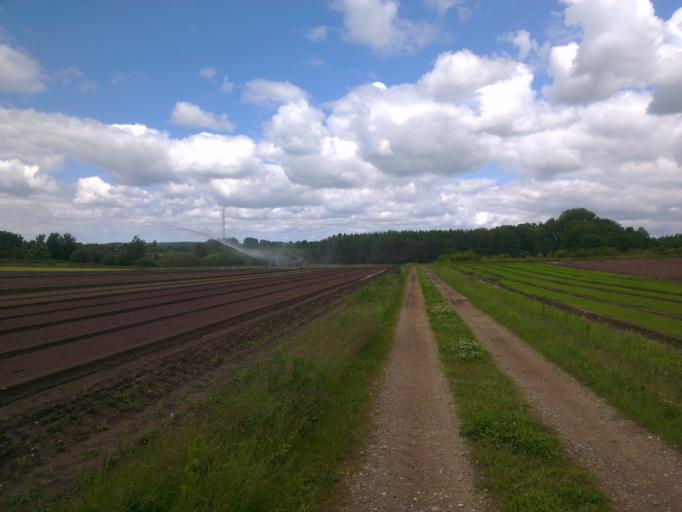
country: DK
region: Capital Region
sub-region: Frederikssund Kommune
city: Frederikssund
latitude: 55.8145
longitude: 12.0264
